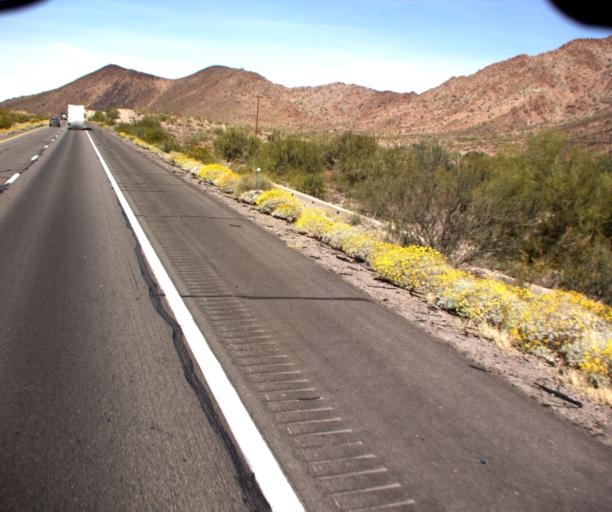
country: US
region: Arizona
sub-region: La Paz County
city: Quartzsite
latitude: 33.6728
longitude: -114.0473
